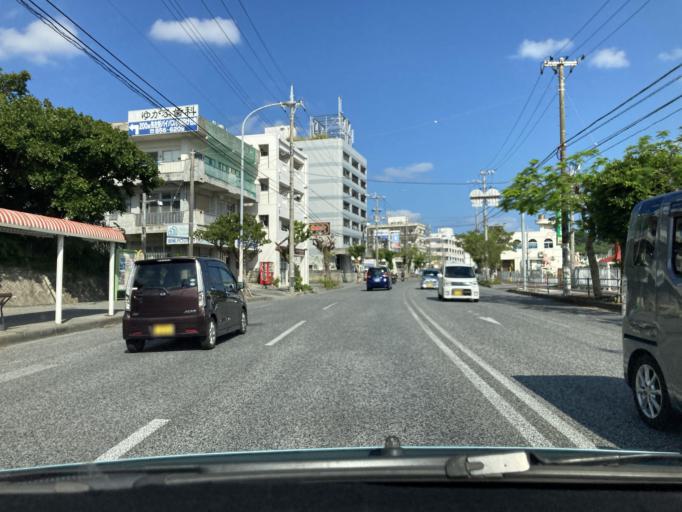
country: JP
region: Okinawa
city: Tomigusuku
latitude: 26.1783
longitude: 127.6814
